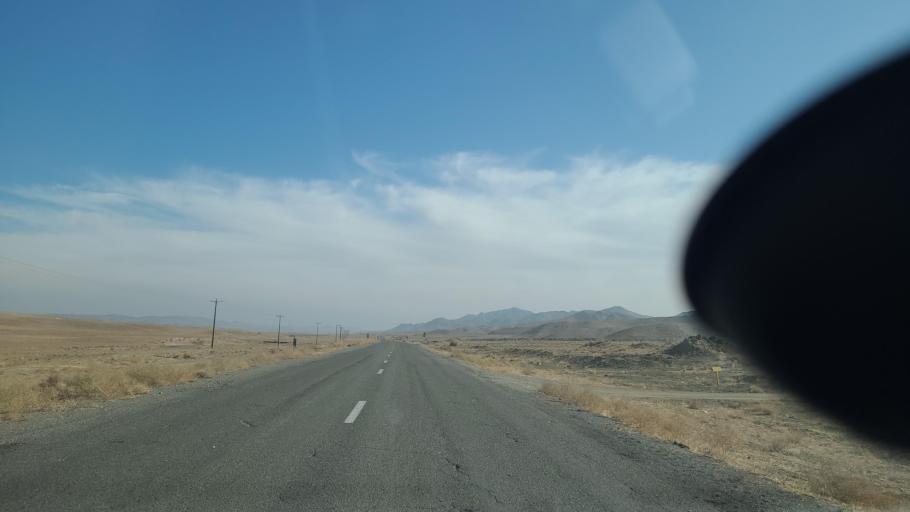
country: IR
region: Razavi Khorasan
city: Fariman
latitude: 35.5887
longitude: 59.6269
